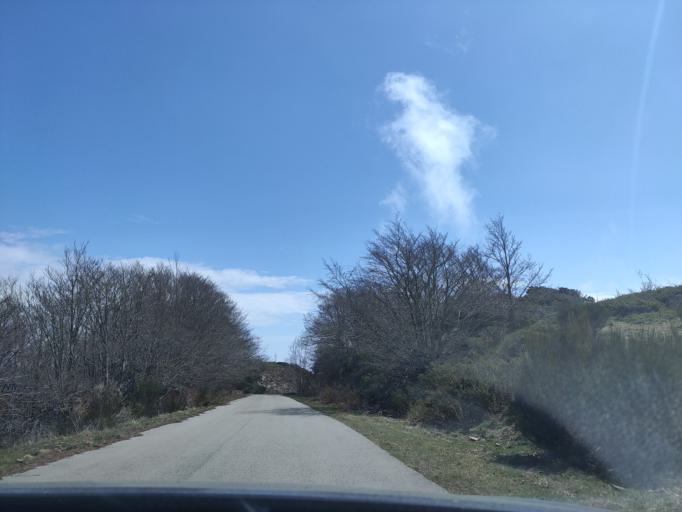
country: ES
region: Catalonia
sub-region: Provincia de Barcelona
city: Fogars de Montclus
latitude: 41.7669
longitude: 2.4521
